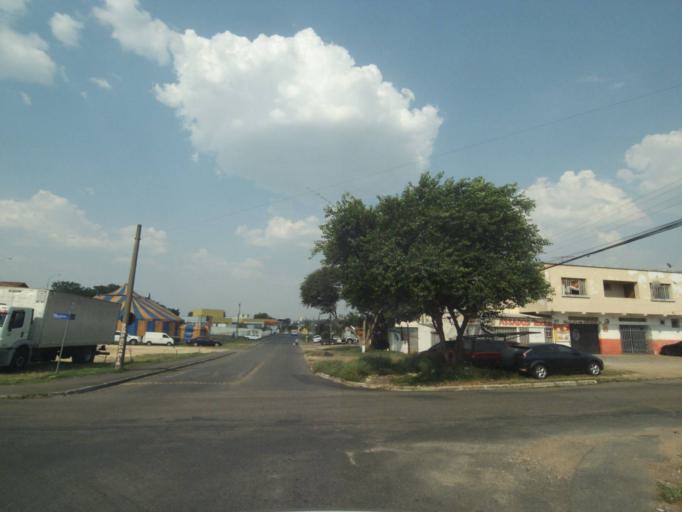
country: BR
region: Parana
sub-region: Sao Jose Dos Pinhais
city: Sao Jose dos Pinhais
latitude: -25.5346
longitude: -49.2413
